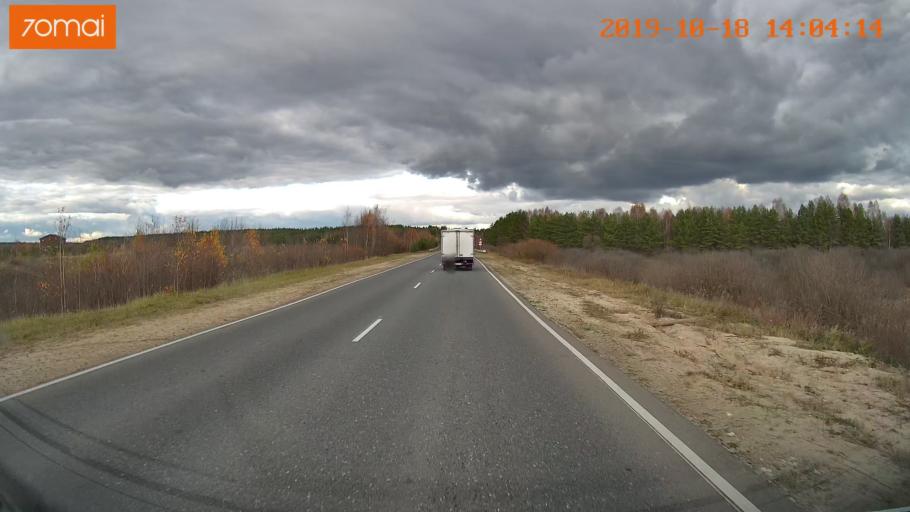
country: RU
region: Rjazan
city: Spas-Klepiki
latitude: 55.1236
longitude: 40.1335
